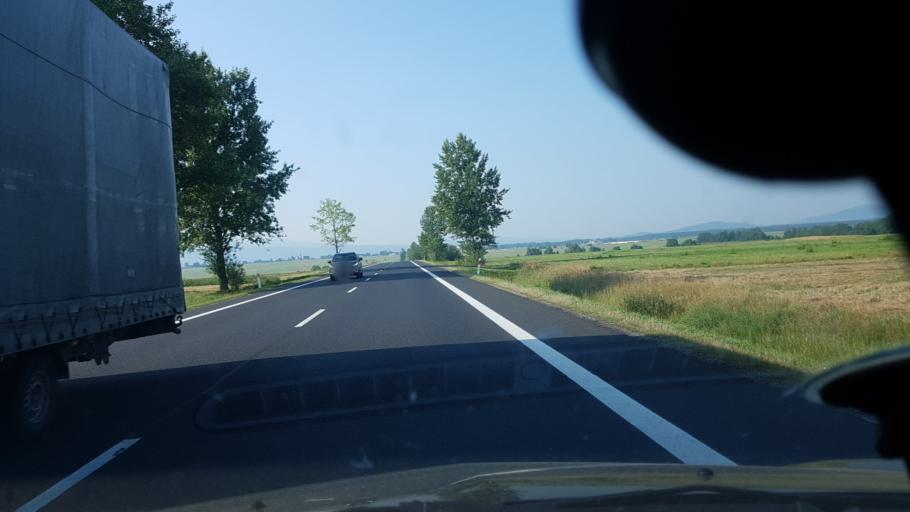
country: PL
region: Lesser Poland Voivodeship
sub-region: Powiat nowotarski
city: Chyzne
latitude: 49.4473
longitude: 19.6851
